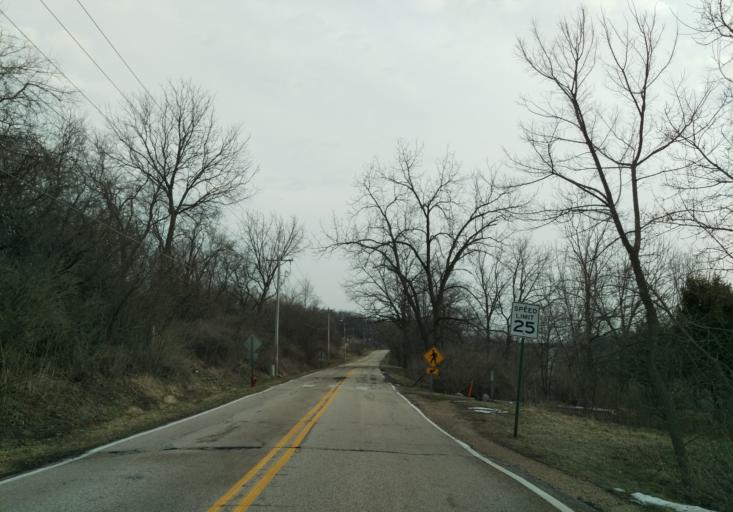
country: US
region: Wisconsin
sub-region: Dane County
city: Middleton
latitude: 43.1080
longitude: -89.4946
